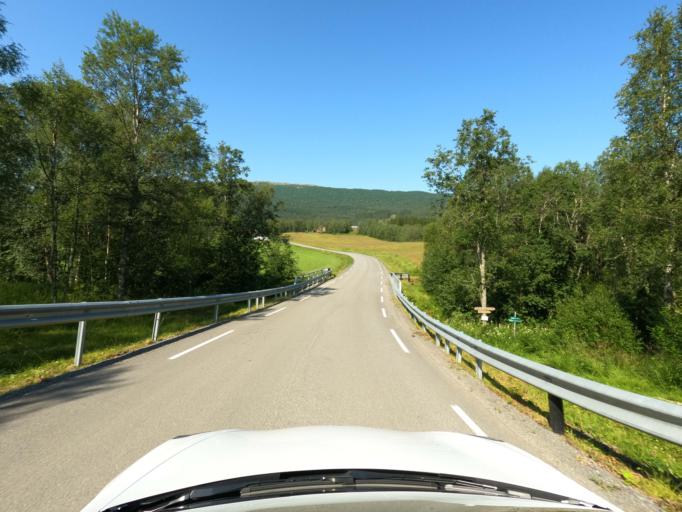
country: NO
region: Nordland
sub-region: Ballangen
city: Ballangen
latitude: 68.3441
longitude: 16.8142
